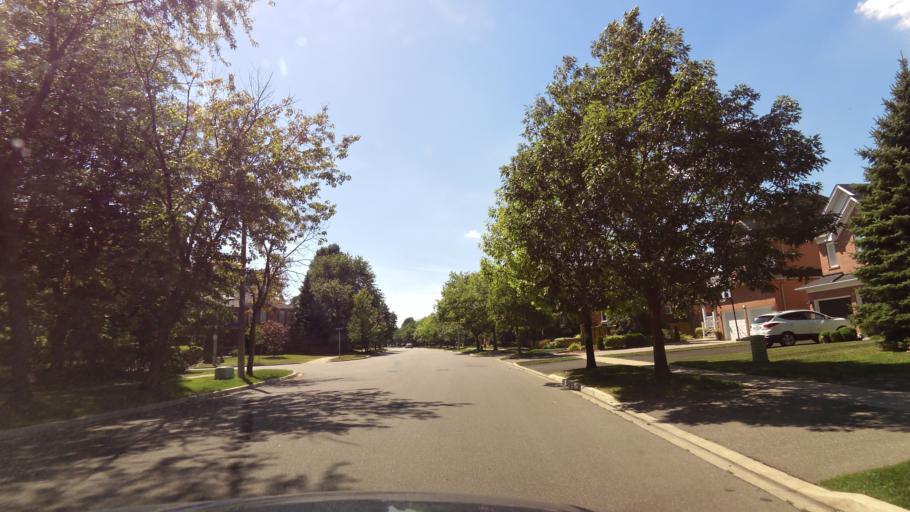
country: CA
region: Ontario
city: Mississauga
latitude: 43.5345
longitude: -79.6081
